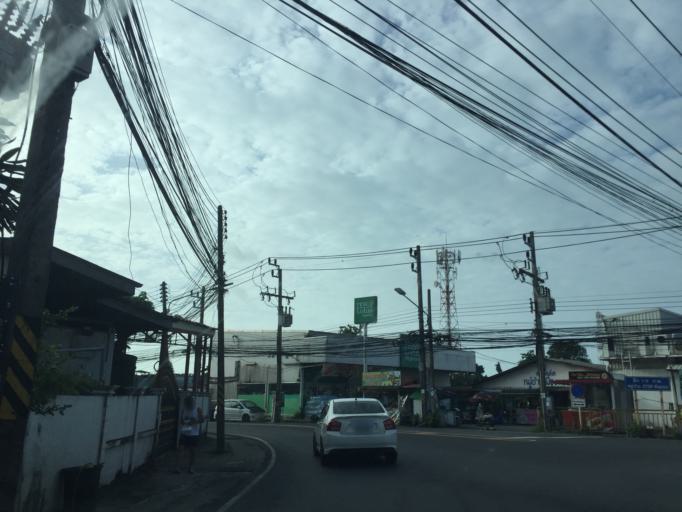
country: TH
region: Phuket
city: Mueang Phuket
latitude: 7.8585
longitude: 98.3776
